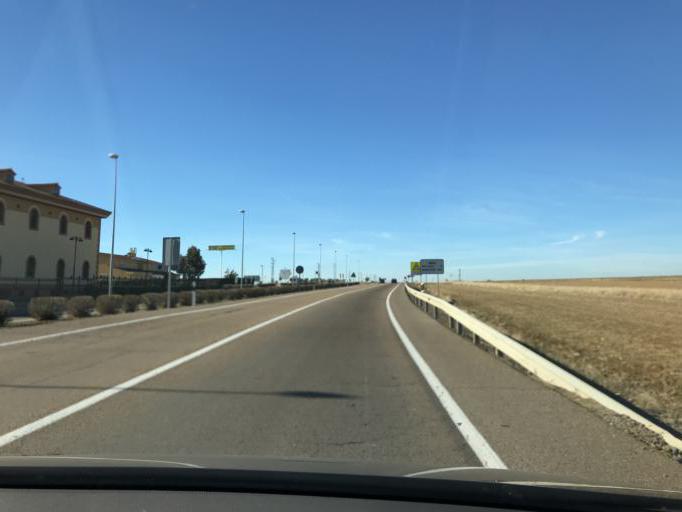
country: ES
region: Extremadura
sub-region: Provincia de Badajoz
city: Azuaga
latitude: 38.2607
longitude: -5.6998
